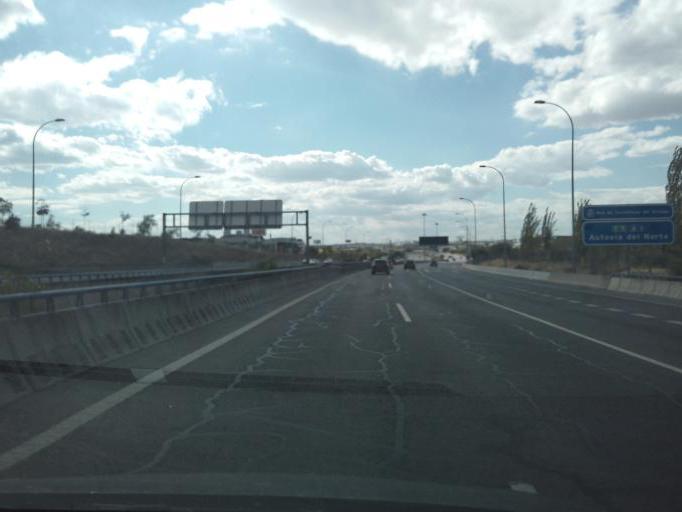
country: ES
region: Madrid
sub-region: Provincia de Madrid
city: San Sebastian de los Reyes
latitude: 40.5318
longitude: -3.6277
